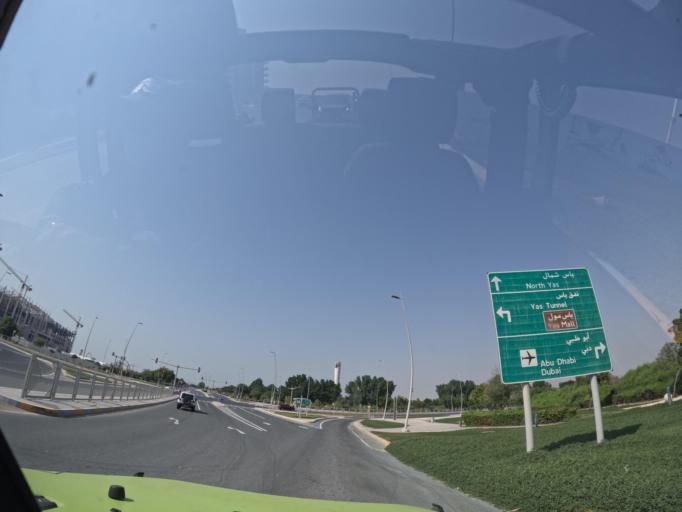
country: AE
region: Abu Dhabi
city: Abu Dhabi
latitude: 24.4835
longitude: 54.6233
